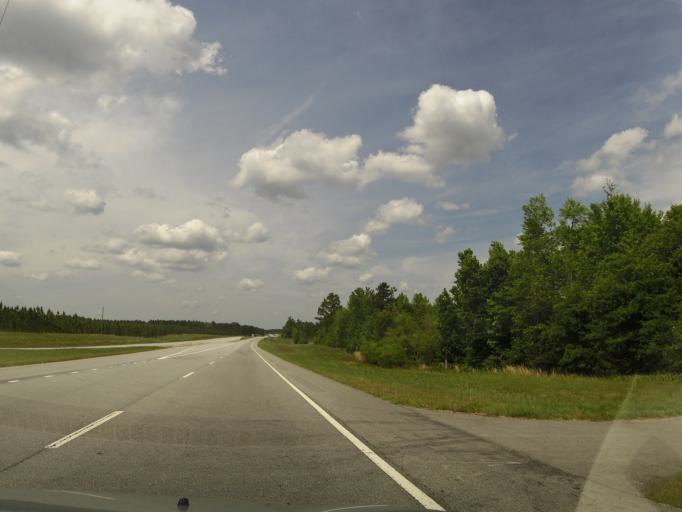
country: US
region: Georgia
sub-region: Emanuel County
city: Swainsboro
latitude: 32.6949
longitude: -82.3904
